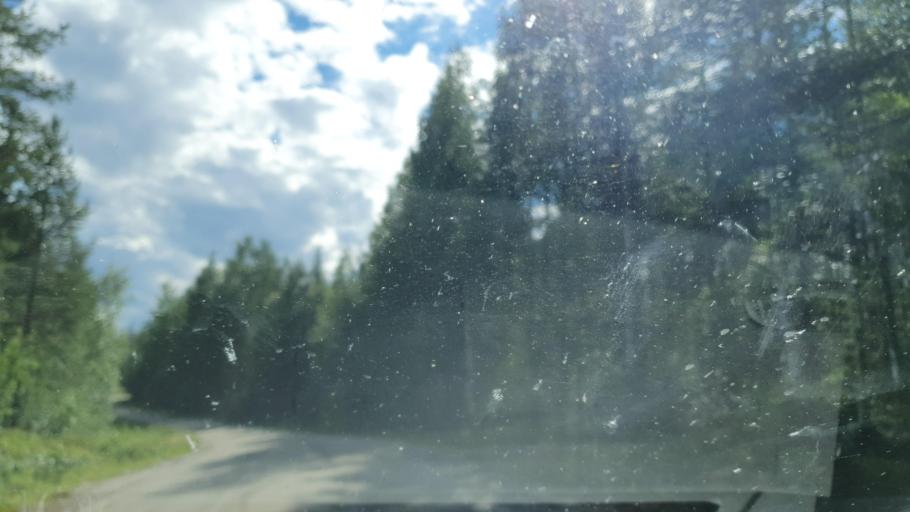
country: FI
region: Kainuu
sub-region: Kehys-Kainuu
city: Kuhmo
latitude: 64.1431
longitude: 29.7027
